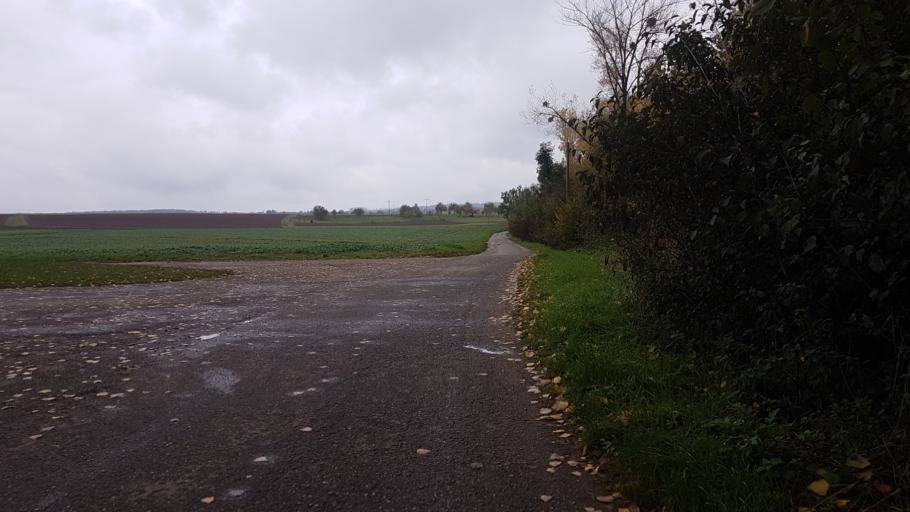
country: DE
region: Baden-Wuerttemberg
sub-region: Tuebingen Region
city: Nehren
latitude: 48.4357
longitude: 9.0531
